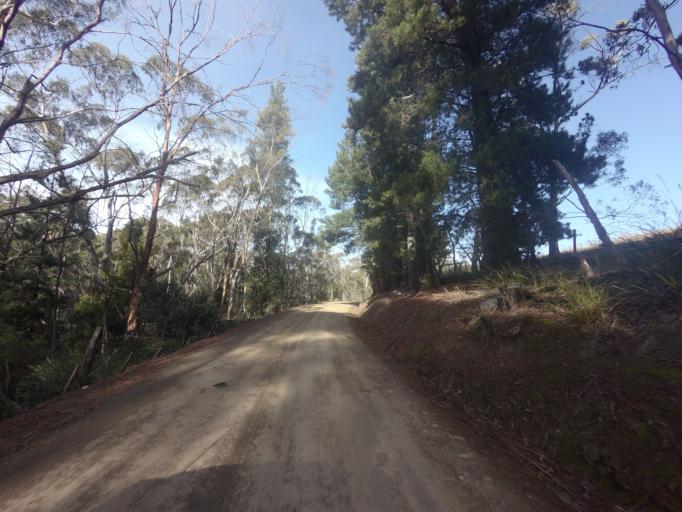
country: AU
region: Tasmania
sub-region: Kingborough
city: Kettering
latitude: -43.1037
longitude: 147.2601
